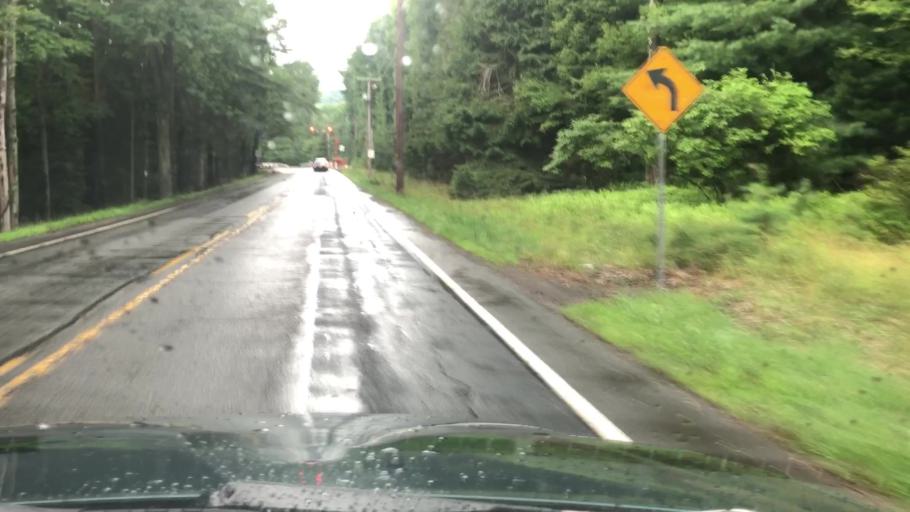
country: US
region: Pennsylvania
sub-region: Monroe County
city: Mountainhome
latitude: 41.2359
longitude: -75.2305
